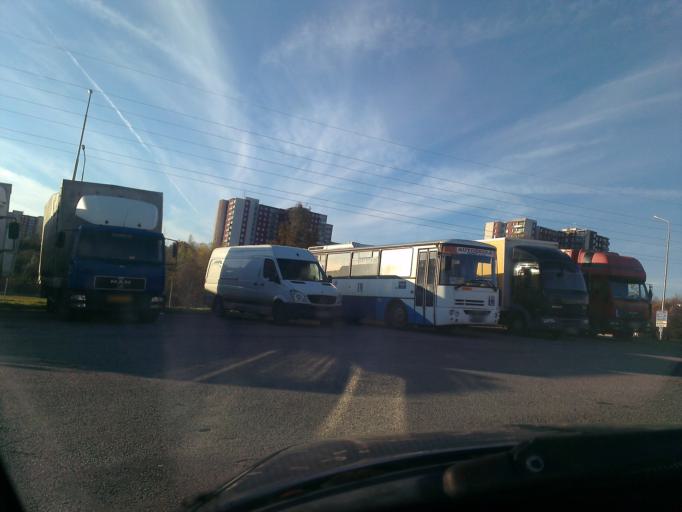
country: CZ
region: South Moravian
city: Bilovice nad Svitavou
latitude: 49.2028
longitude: 16.6673
